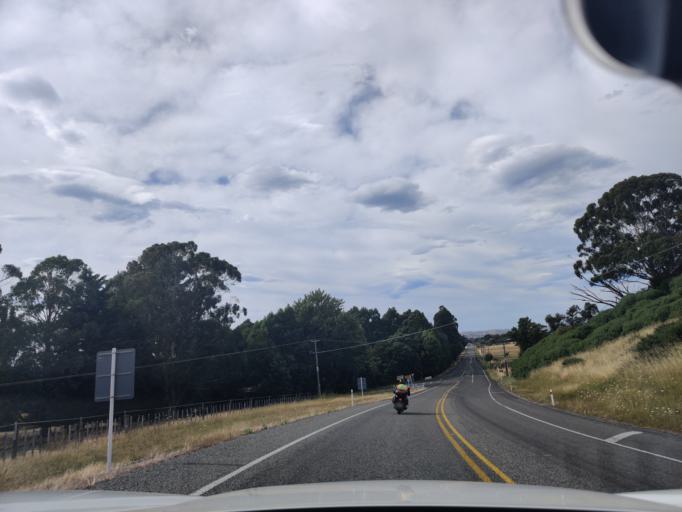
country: NZ
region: Wellington
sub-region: Masterton District
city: Masterton
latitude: -40.8815
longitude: 175.6579
